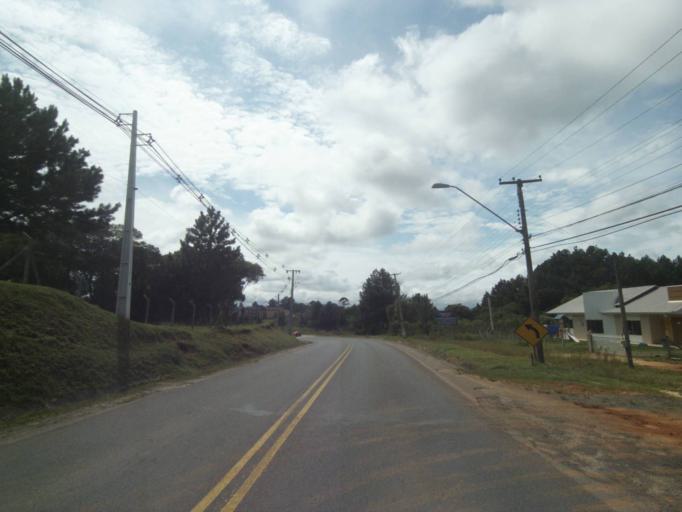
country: BR
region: Parana
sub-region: Campina Grande Do Sul
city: Campina Grande do Sul
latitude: -25.3099
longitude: -49.0630
